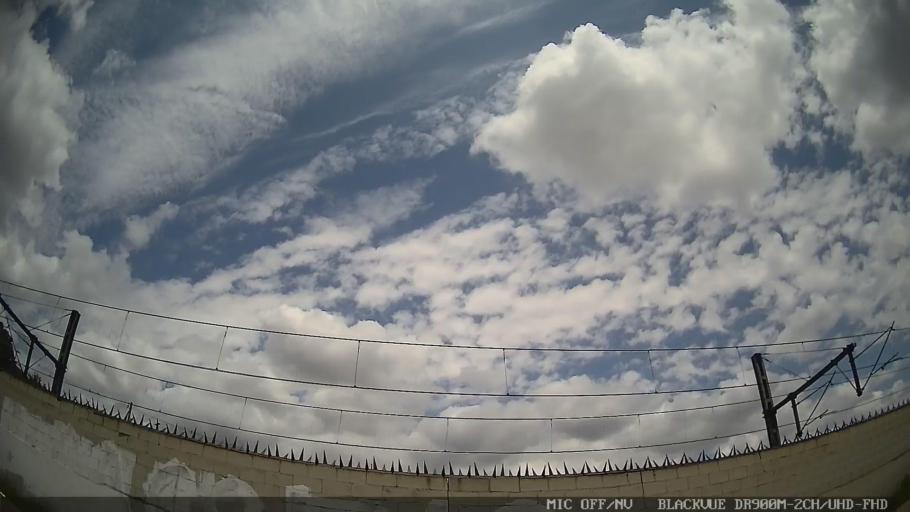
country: BR
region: Sao Paulo
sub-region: Ferraz De Vasconcelos
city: Ferraz de Vasconcelos
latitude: -23.5411
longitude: -46.4655
